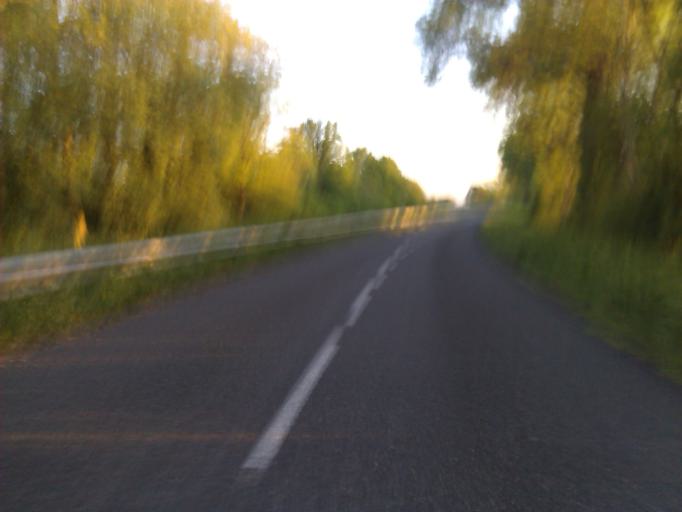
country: FR
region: Bourgogne
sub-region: Departement de Saone-et-Loire
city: Paray-le-Monial
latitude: 46.4618
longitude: 4.1619
